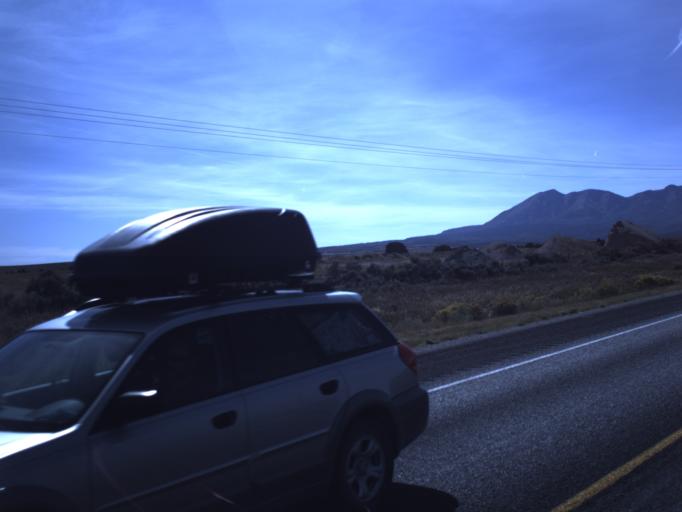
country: US
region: Utah
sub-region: San Juan County
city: Monticello
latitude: 37.8729
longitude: -109.2858
